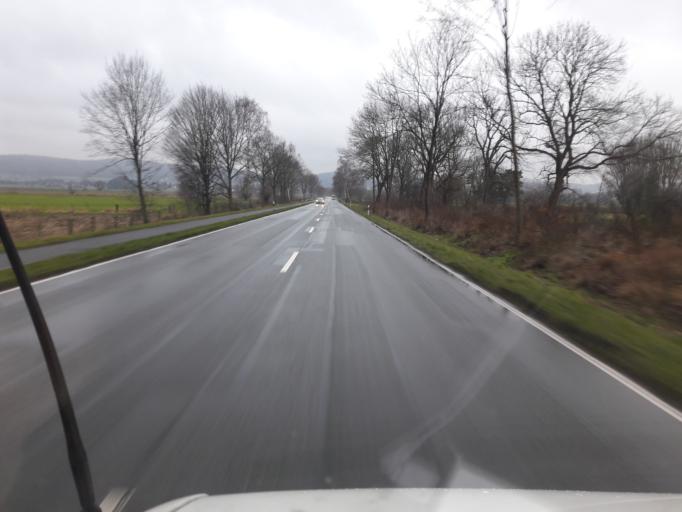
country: DE
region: North Rhine-Westphalia
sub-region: Regierungsbezirk Detmold
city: Hille
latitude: 52.3027
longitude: 8.8093
